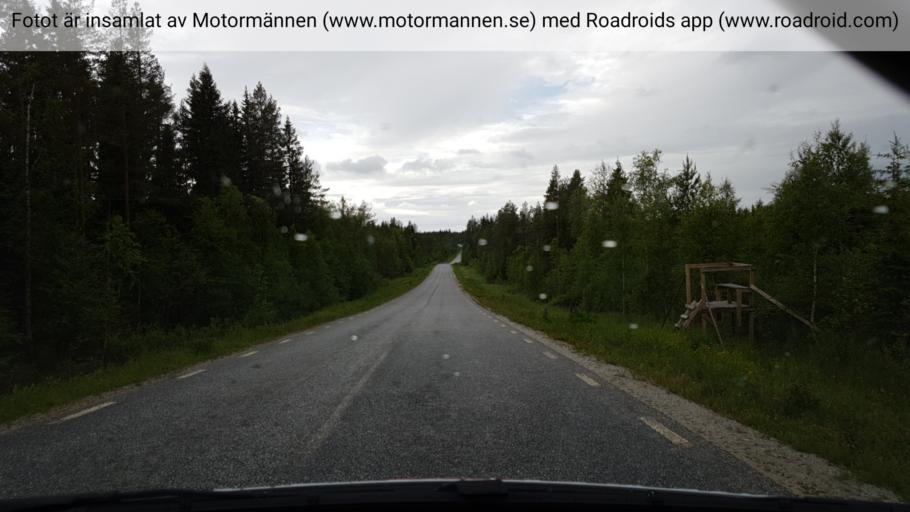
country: SE
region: Vaesterbotten
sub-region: Bjurholms Kommun
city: Bjurholm
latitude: 63.9808
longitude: 19.3306
